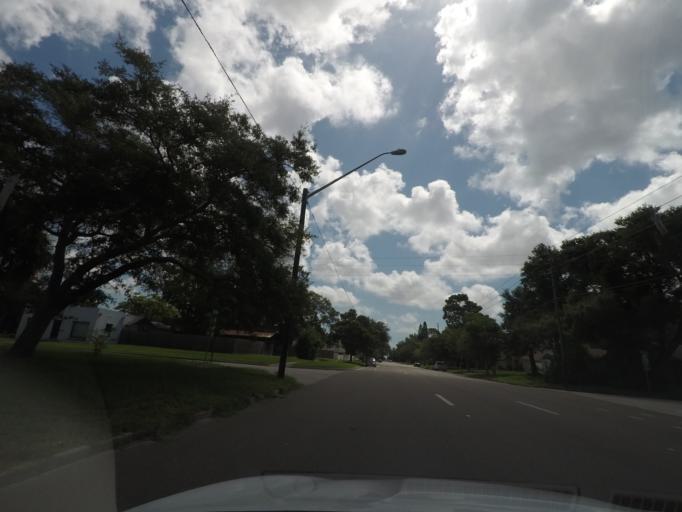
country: US
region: Florida
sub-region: Pinellas County
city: Gulfport
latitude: 27.7701
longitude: -82.7083
